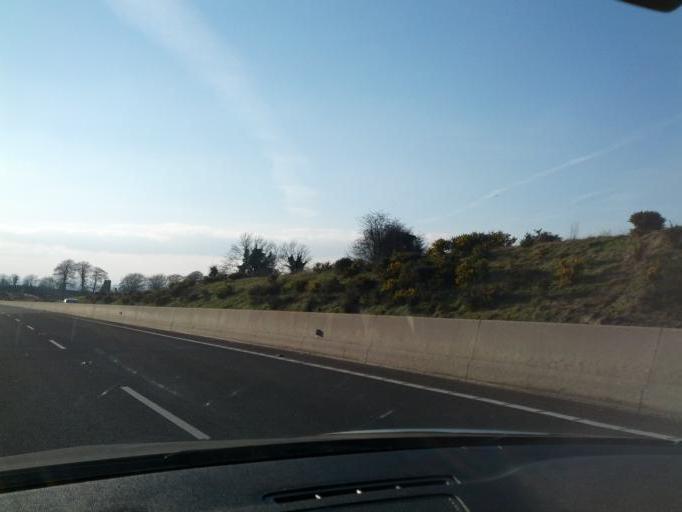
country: IE
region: Munster
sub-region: North Tipperary
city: Roscrea
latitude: 52.9095
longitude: -7.8650
